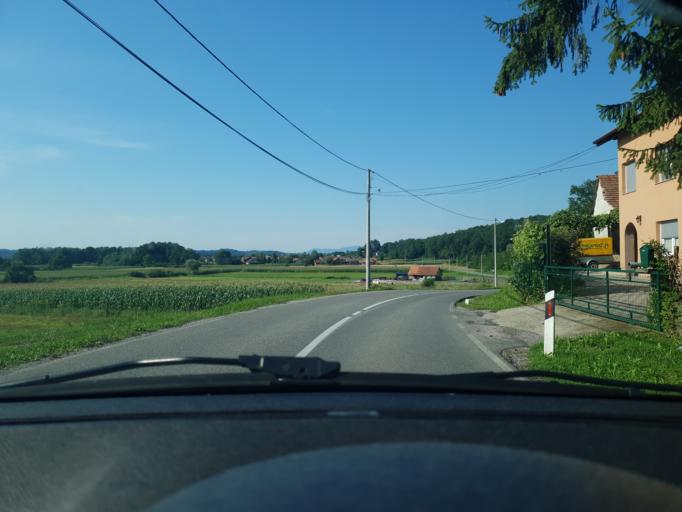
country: HR
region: Zagrebacka
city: Jakovlje
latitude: 45.9178
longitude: 15.8422
